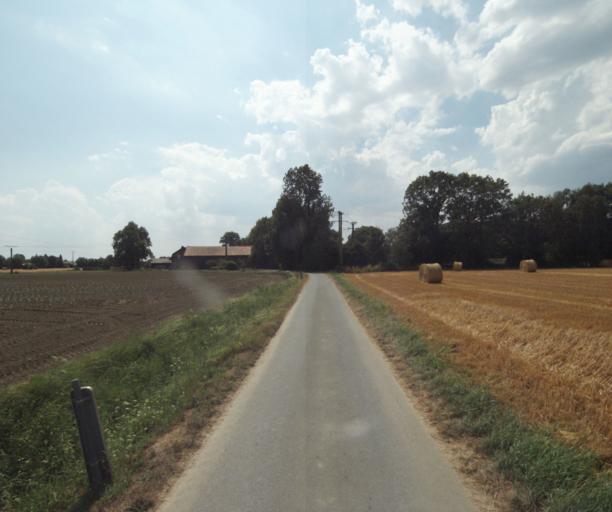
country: FR
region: Nord-Pas-de-Calais
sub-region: Departement du Nord
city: Comines
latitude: 50.7500
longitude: 3.0040
